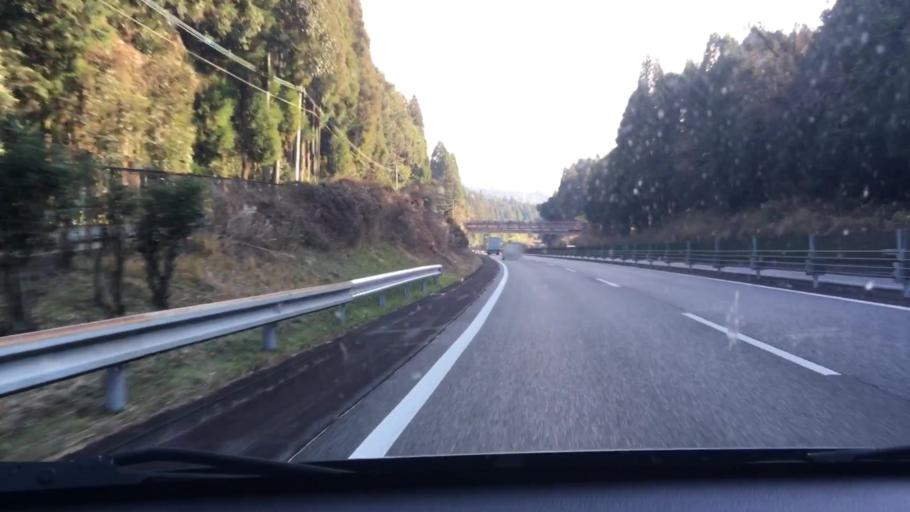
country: JP
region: Kagoshima
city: Okuchi-shinohara
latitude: 32.0031
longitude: 130.7565
